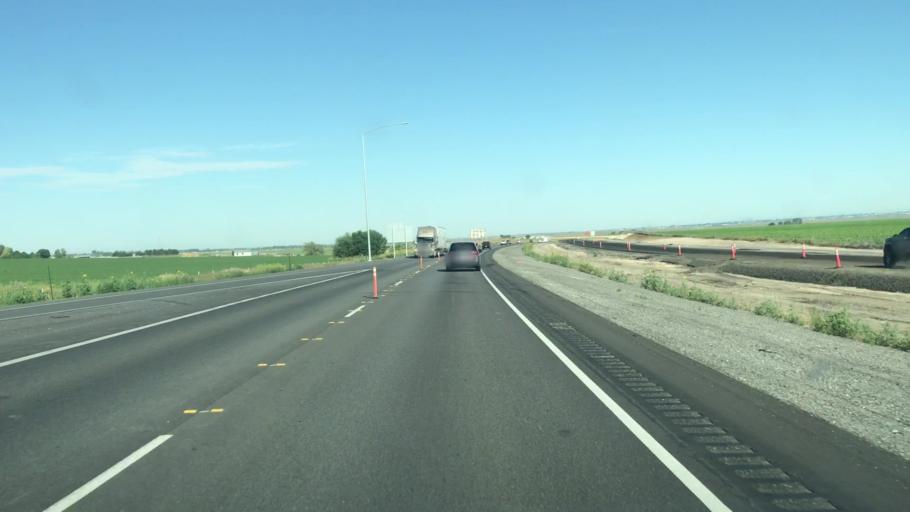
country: US
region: Idaho
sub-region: Twin Falls County
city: Hansen
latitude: 42.5780
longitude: -114.3002
